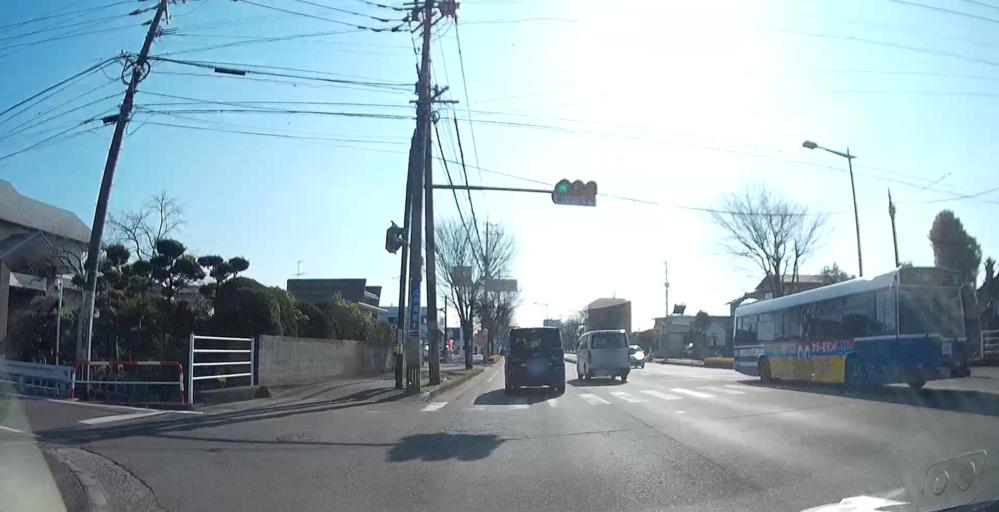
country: JP
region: Kumamoto
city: Kumamoto
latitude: 32.7786
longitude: 130.6732
